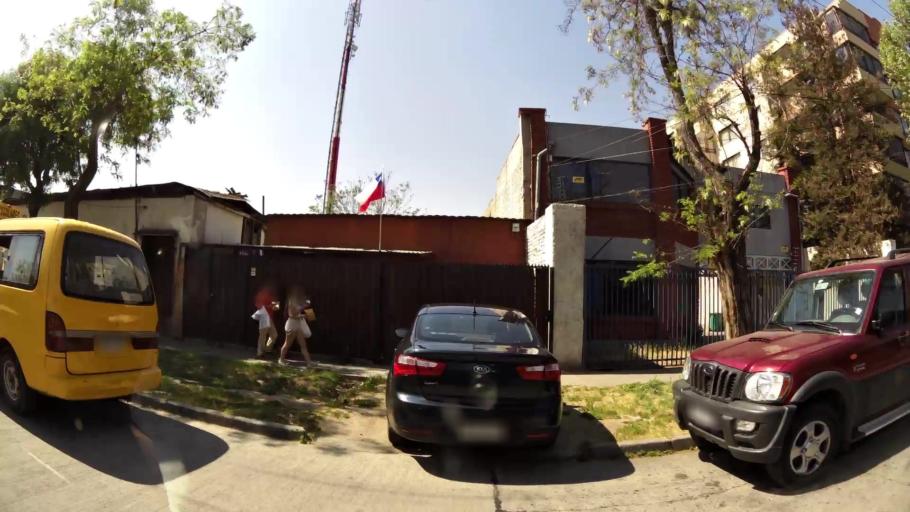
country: CL
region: Santiago Metropolitan
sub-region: Provincia de Maipo
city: San Bernardo
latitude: -33.5946
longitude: -70.7090
